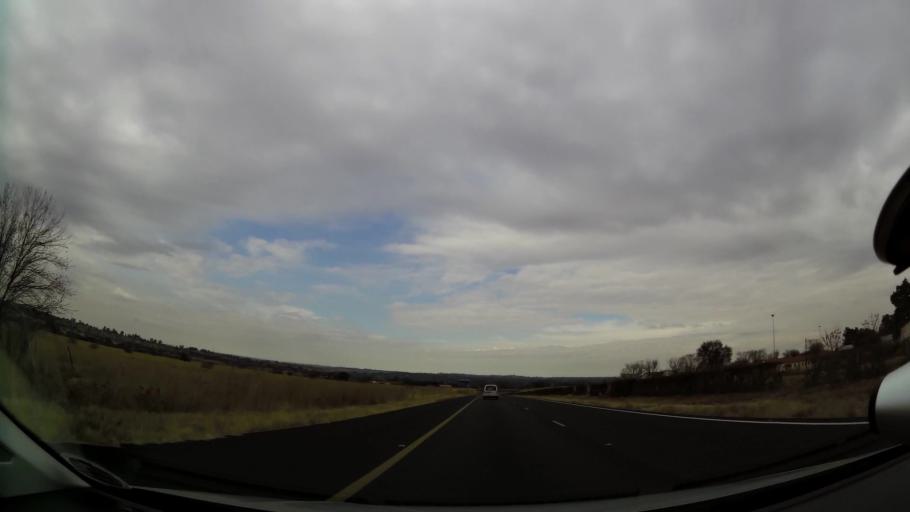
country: ZA
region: Orange Free State
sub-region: Fezile Dabi District Municipality
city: Kroonstad
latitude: -27.6423
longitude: 27.2477
